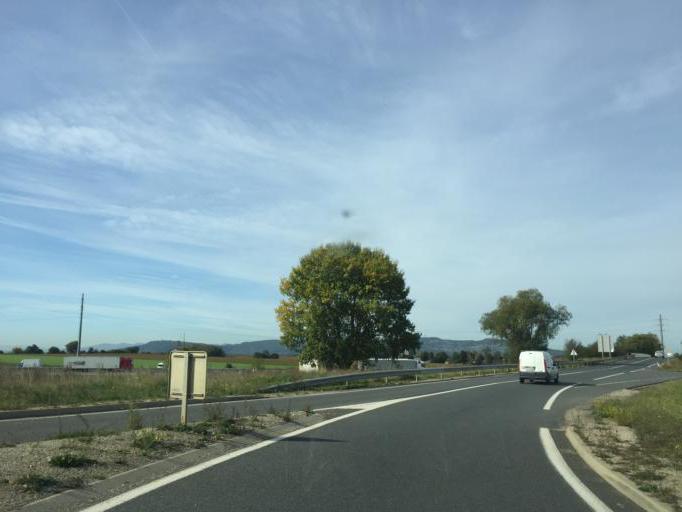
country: FR
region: Rhone-Alpes
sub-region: Departement de l'Ain
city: Mionnay
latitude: 45.8821
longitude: 4.8998
